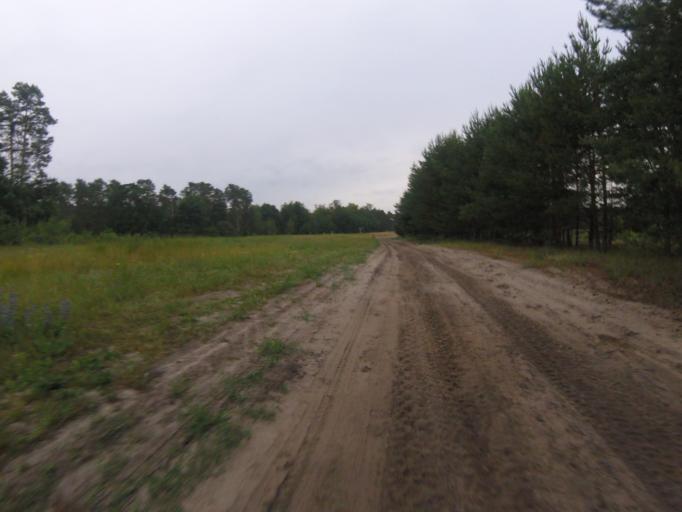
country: DE
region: Brandenburg
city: Gross Koris
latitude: 52.1951
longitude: 13.6466
